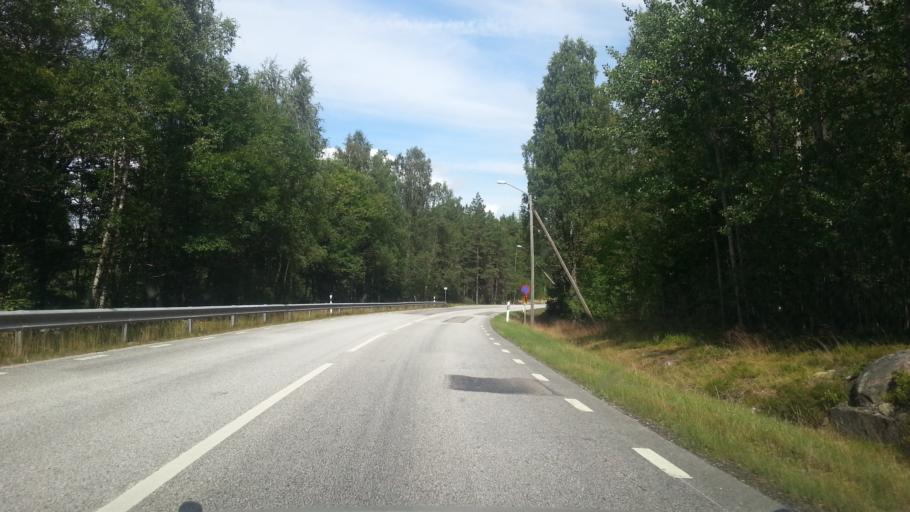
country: SE
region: Vaestmanland
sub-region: Skinnskattebergs Kommun
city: Skinnskatteberg
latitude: 59.8138
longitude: 15.5277
